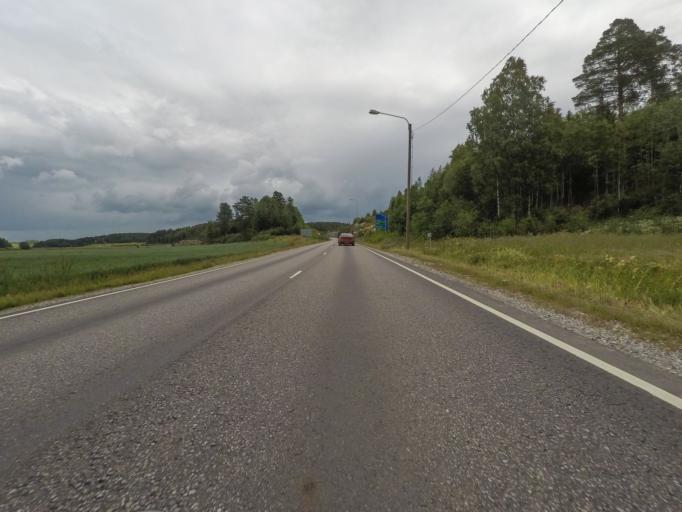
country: FI
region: Varsinais-Suomi
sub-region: Salo
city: Muurla
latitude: 60.3753
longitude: 23.3157
